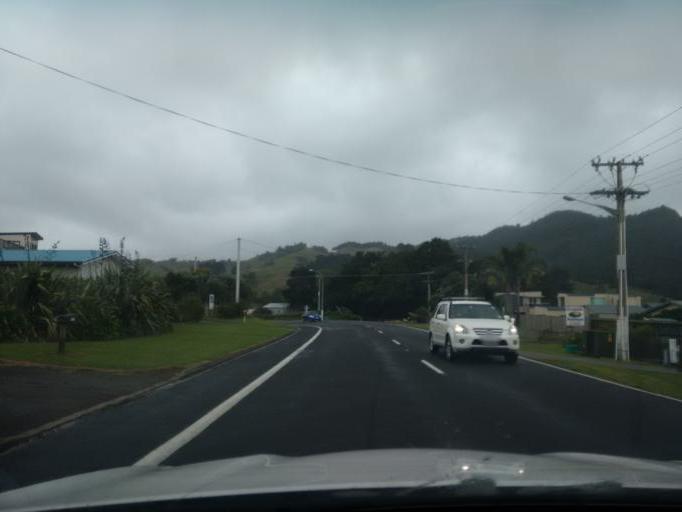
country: NZ
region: Waikato
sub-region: Thames-Coromandel District
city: Whitianga
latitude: -36.7935
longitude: 175.7249
